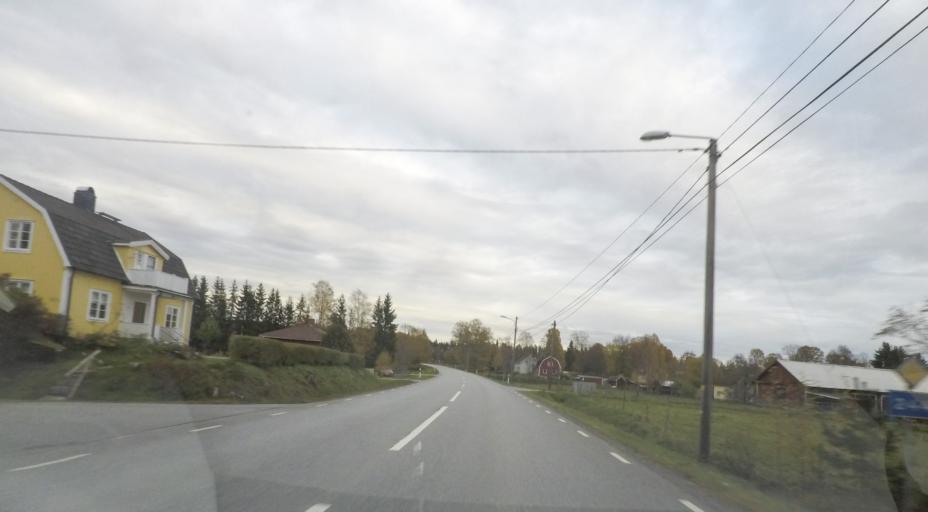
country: SE
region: OErebro
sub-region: Nora Kommun
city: As
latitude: 59.5187
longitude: 14.9119
